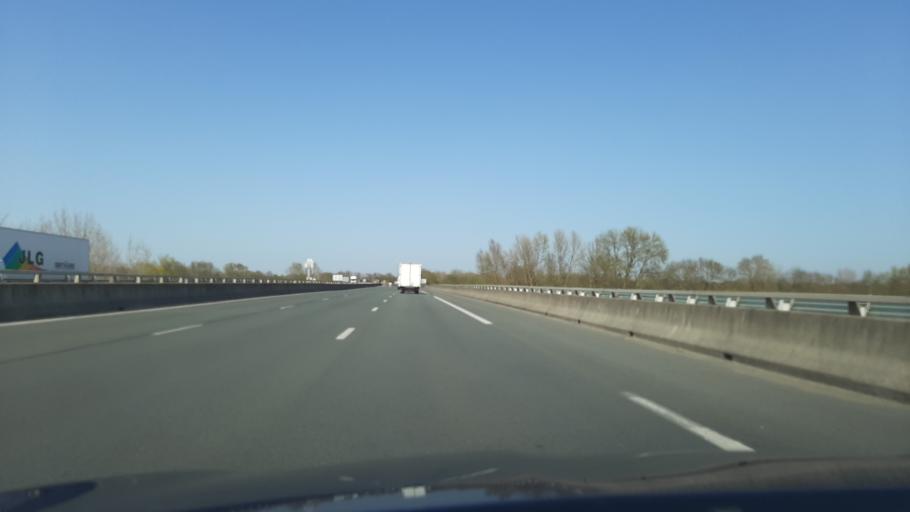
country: FR
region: Pays de la Loire
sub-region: Departement de Maine-et-Loire
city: Les Ponts-de-Ce
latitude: 47.4191
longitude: -0.5058
